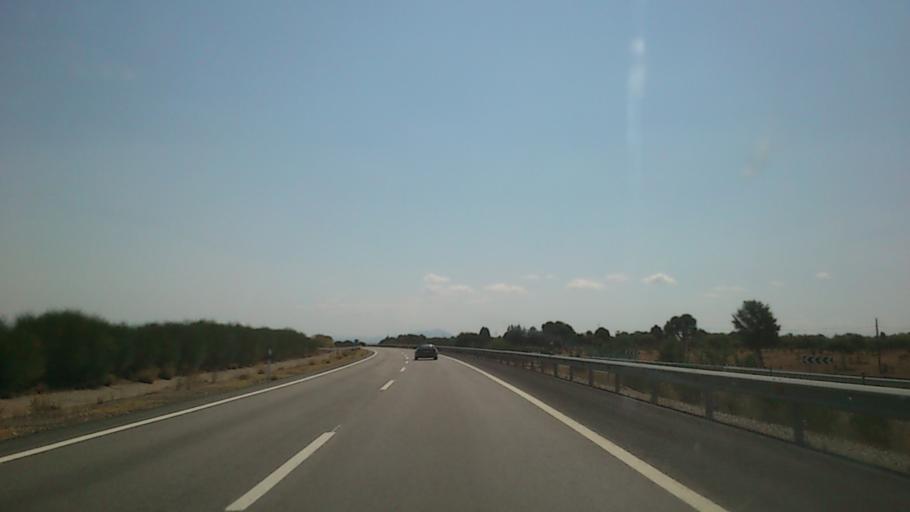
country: ES
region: Aragon
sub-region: Provincia de Teruel
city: Valbona
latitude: 40.1902
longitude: -0.9059
